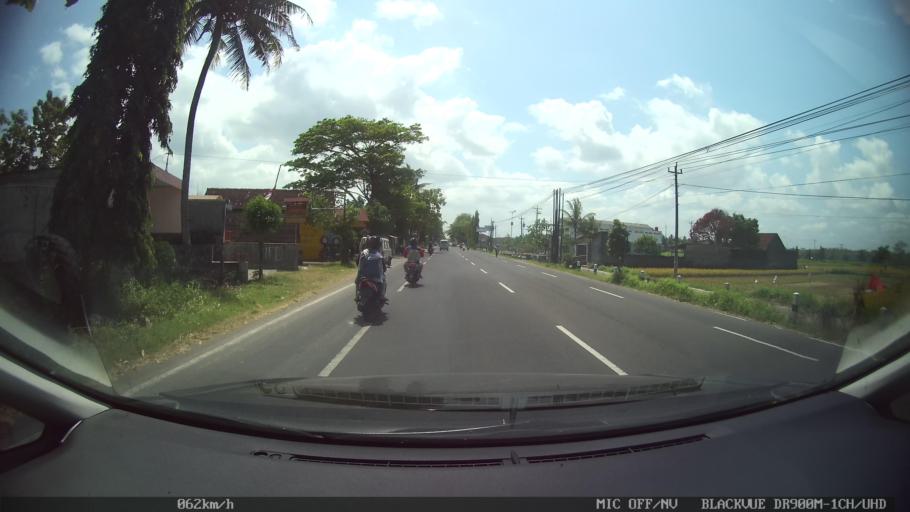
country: ID
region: Daerah Istimewa Yogyakarta
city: Pandak
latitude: -7.9225
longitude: 110.2808
